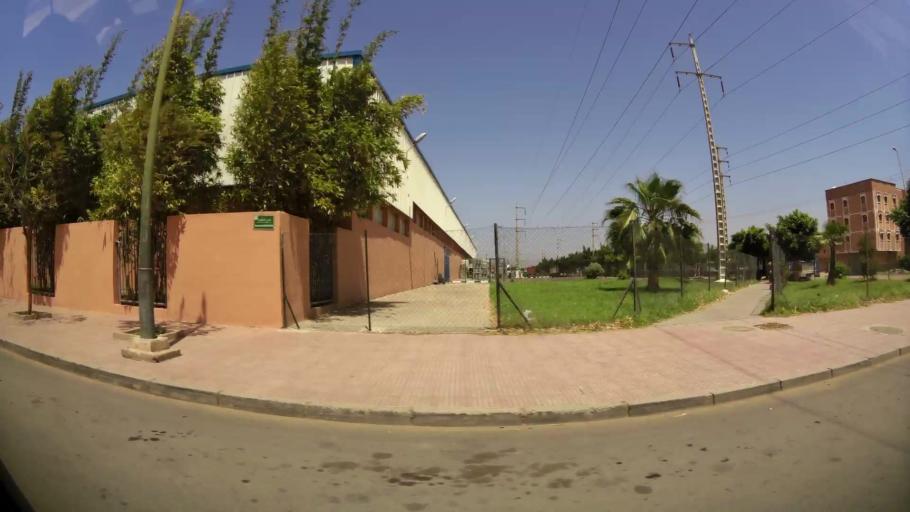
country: MA
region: Souss-Massa-Draa
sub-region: Inezgane-Ait Mellou
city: Inezgane
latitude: 30.3435
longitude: -9.4906
